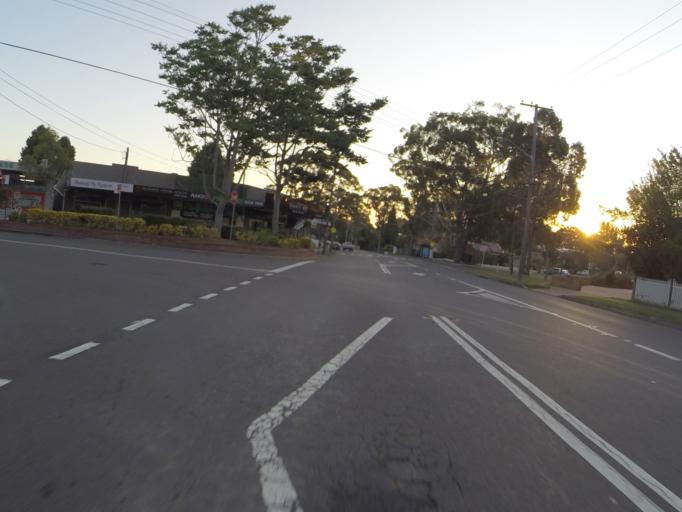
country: AU
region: New South Wales
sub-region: Hurstville
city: Peakhurst
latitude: -33.9637
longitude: 151.0568
